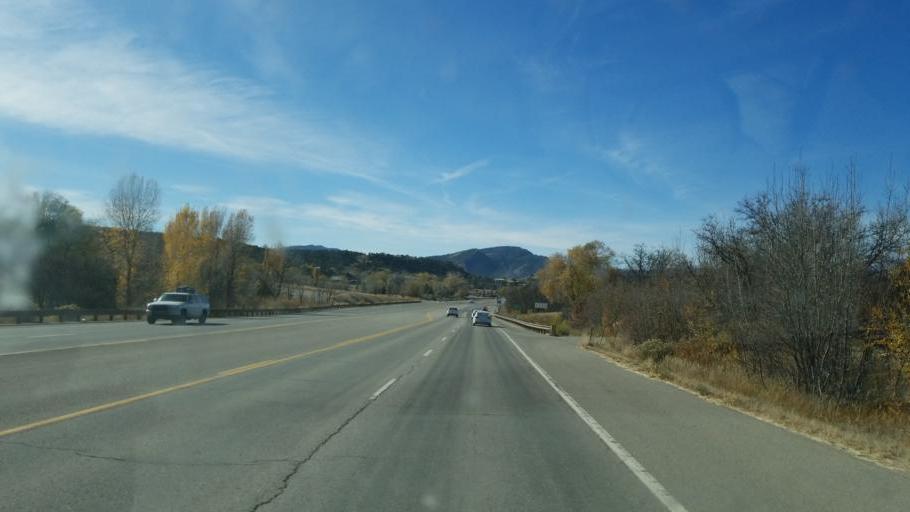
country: US
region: Colorado
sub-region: La Plata County
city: Durango
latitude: 37.2271
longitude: -107.8162
